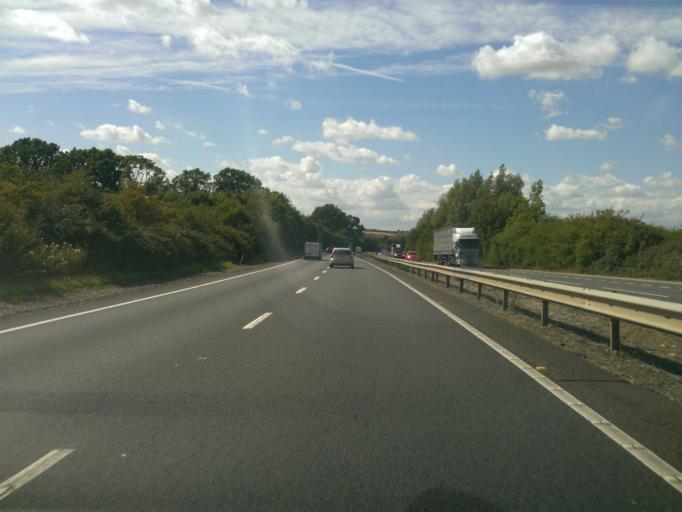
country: GB
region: England
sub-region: Northamptonshire
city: Thrapston
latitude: 52.3841
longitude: -0.4901
